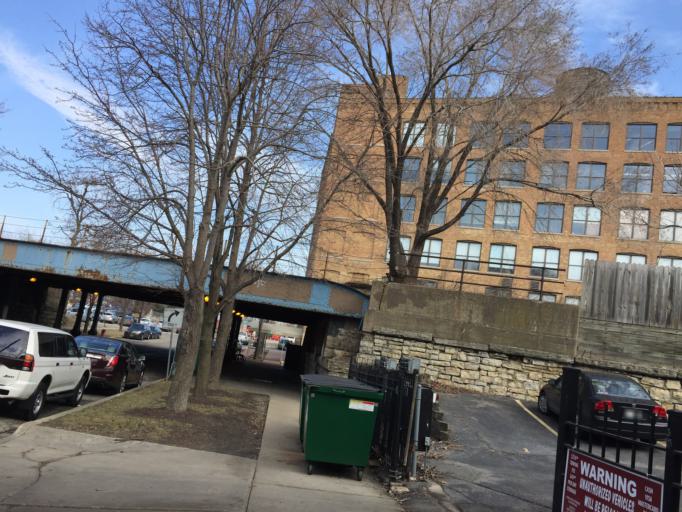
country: US
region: Illinois
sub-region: Cook County
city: Chicago
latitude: 41.8976
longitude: -87.6518
